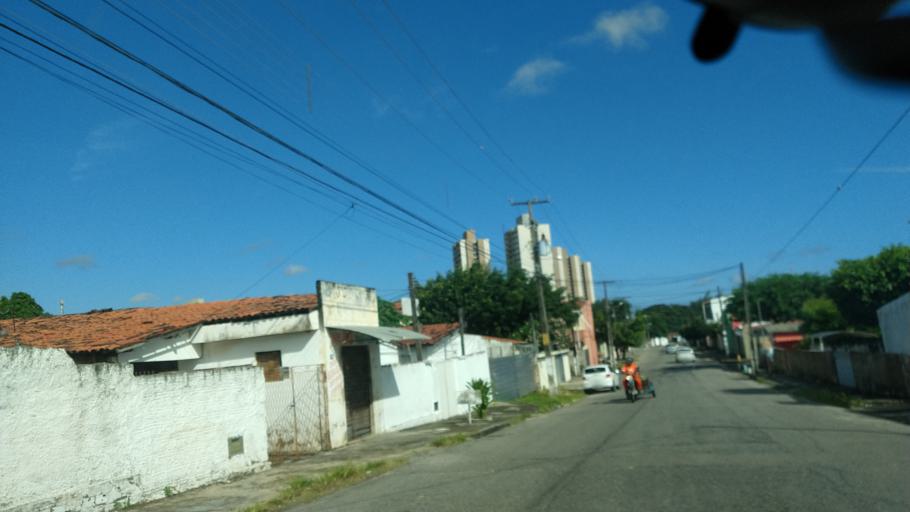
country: BR
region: Rio Grande do Norte
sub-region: Natal
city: Natal
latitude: -5.8620
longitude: -35.2077
